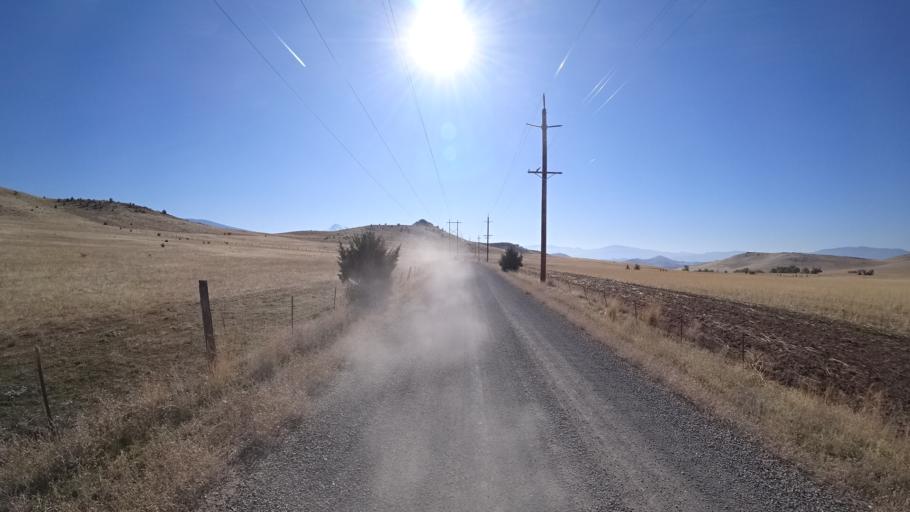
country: US
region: California
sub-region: Siskiyou County
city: Montague
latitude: 41.7509
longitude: -122.3595
